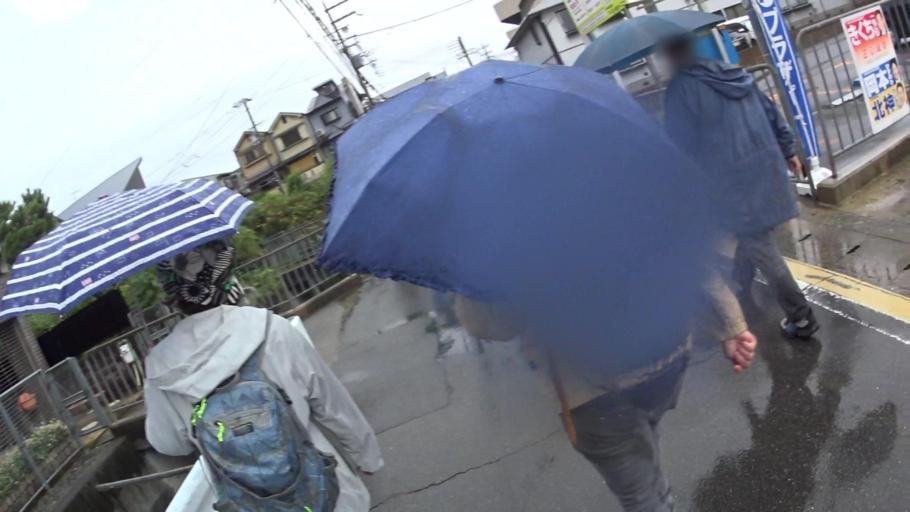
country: JP
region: Kyoto
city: Muko
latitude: 35.0105
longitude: 135.7051
